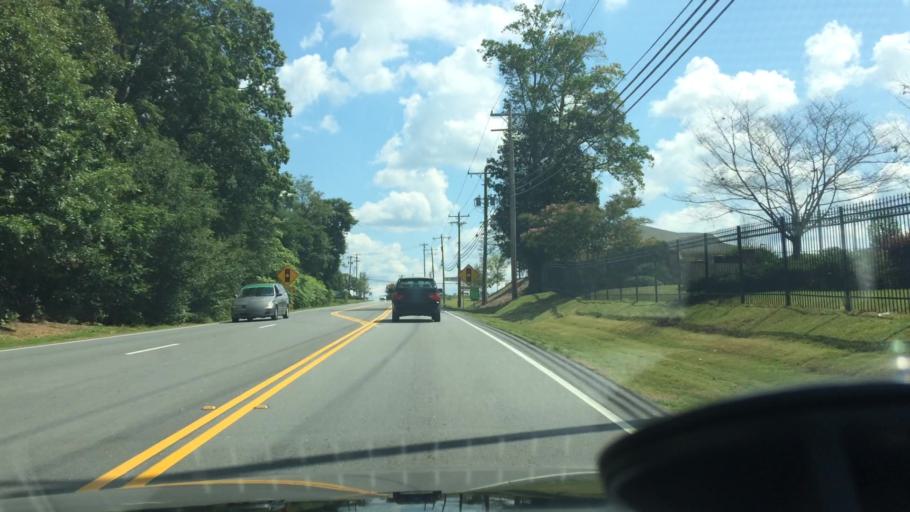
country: US
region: South Carolina
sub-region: Greenville County
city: Sans Souci
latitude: 34.9136
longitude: -82.4320
